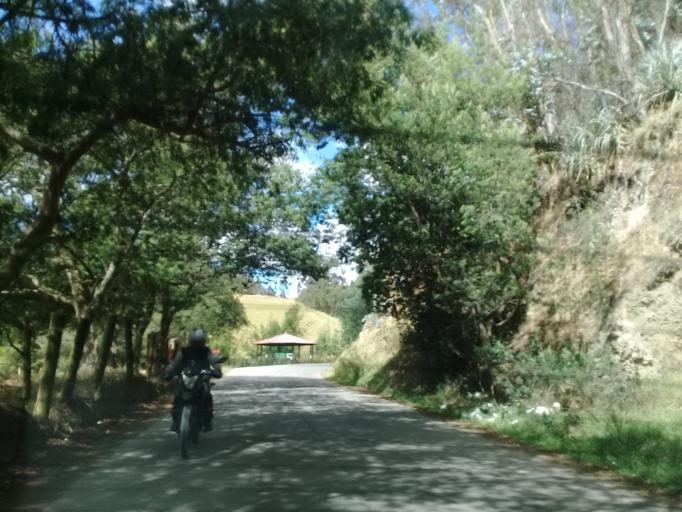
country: CO
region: Cundinamarca
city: Choconta
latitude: 5.1488
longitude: -73.6982
